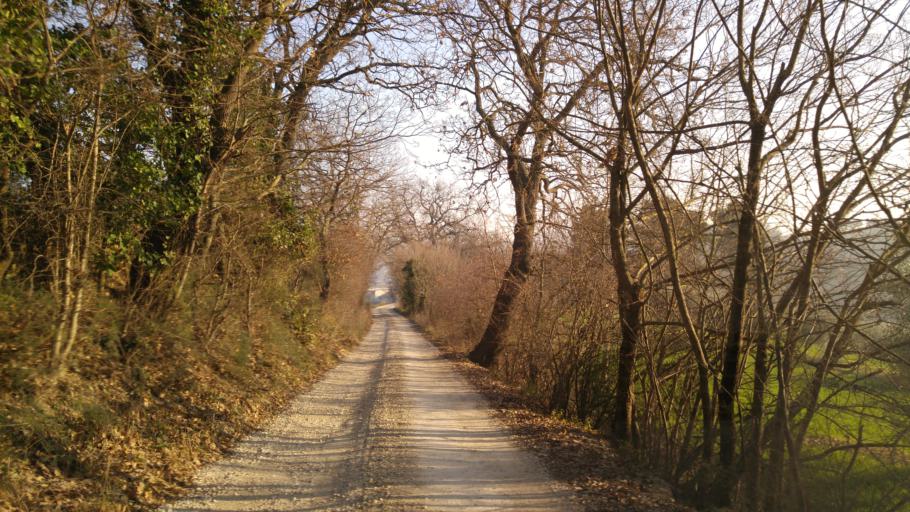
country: IT
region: The Marches
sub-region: Provincia di Pesaro e Urbino
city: Fenile
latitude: 43.8502
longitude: 12.9647
